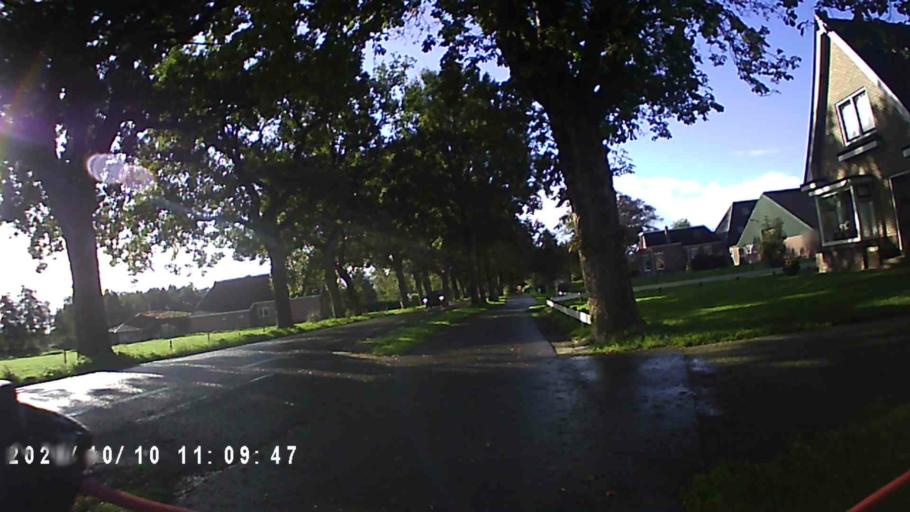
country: NL
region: Friesland
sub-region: Gemeente Smallingerland
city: Drachtstercompagnie
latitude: 53.1175
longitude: 6.2071
